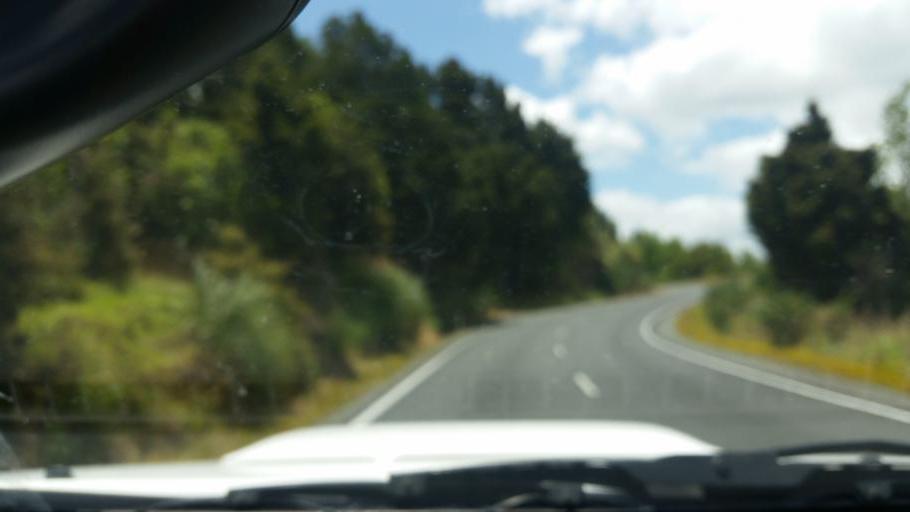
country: NZ
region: Northland
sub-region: Whangarei
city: Ruakaka
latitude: -36.0841
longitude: 174.2396
